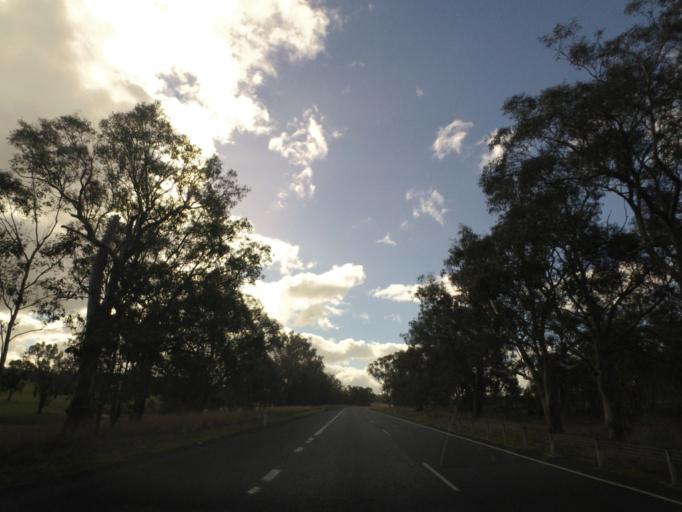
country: AU
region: New South Wales
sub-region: Greater Hume Shire
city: Holbrook
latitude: -35.8655
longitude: 147.1863
